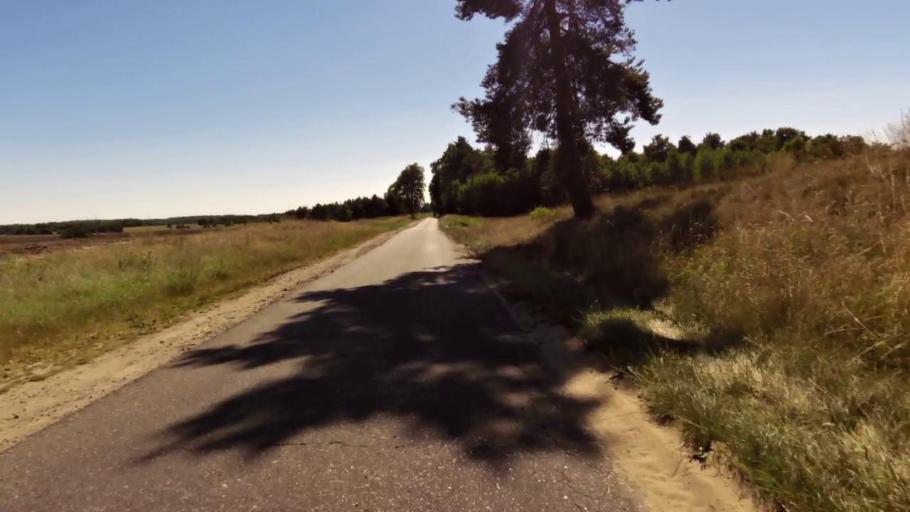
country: PL
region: West Pomeranian Voivodeship
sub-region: Powiat szczecinecki
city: Szczecinek
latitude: 53.6964
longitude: 16.6069
